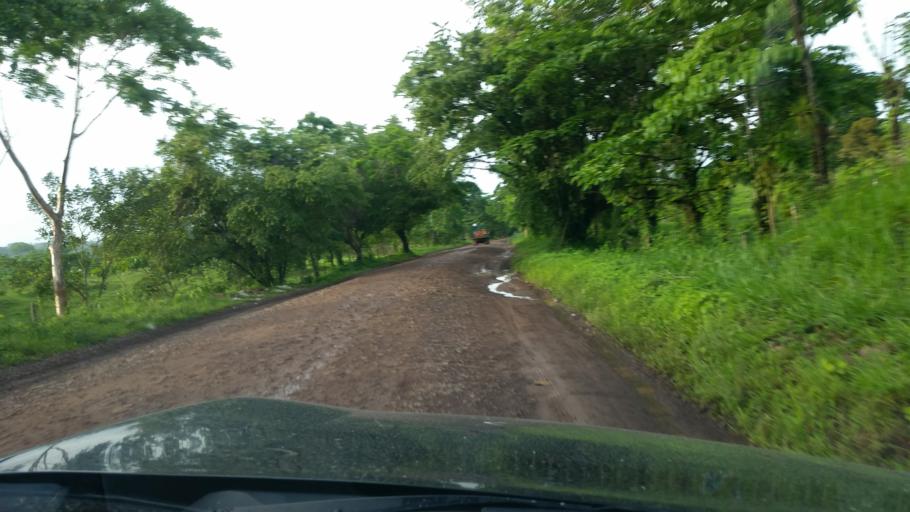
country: NI
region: Atlantico Norte (RAAN)
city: Siuna
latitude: 13.3040
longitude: -84.9100
